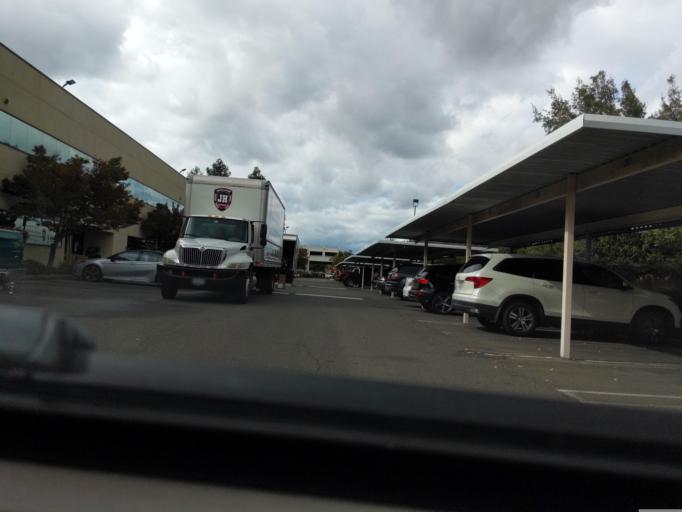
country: US
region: California
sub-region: Stanislaus County
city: Modesto
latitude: 37.6707
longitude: -120.9715
